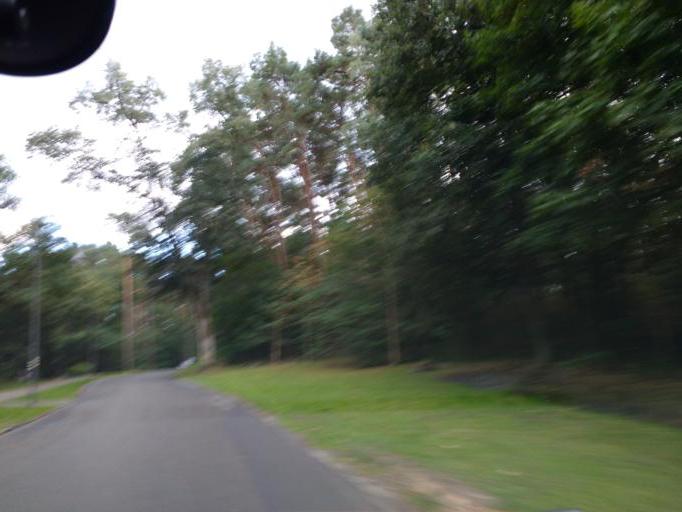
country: DE
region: Brandenburg
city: Bad Saarow
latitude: 52.2786
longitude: 14.0393
